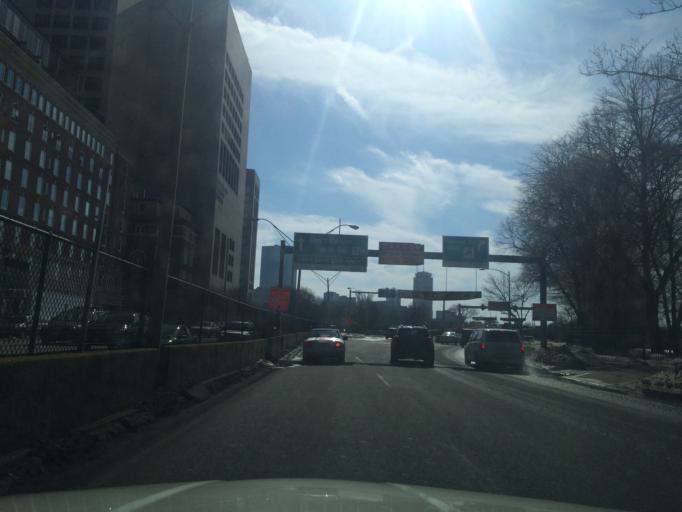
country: US
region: Massachusetts
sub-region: Suffolk County
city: Boston
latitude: 42.3641
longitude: -71.0701
